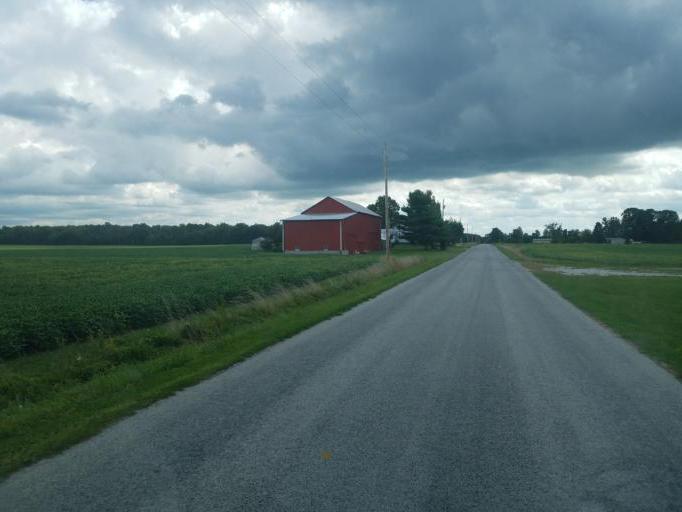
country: US
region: Ohio
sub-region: Huron County
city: Greenwich
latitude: 41.0062
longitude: -82.5347
